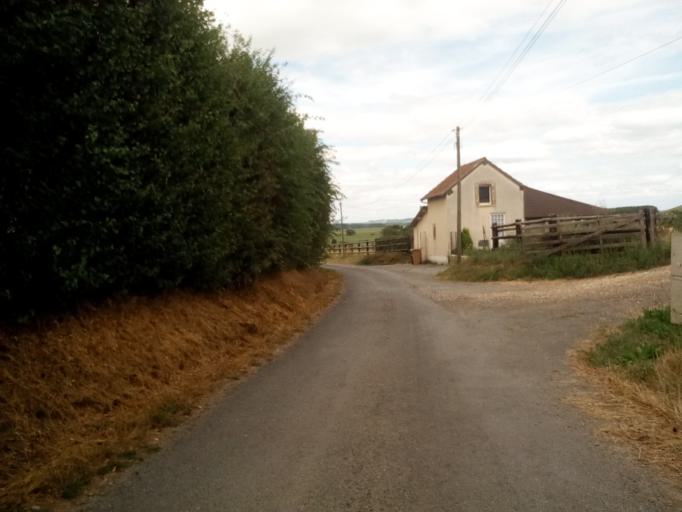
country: FR
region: Lower Normandy
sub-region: Departement du Calvados
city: Troarn
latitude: 49.1703
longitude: -0.1649
